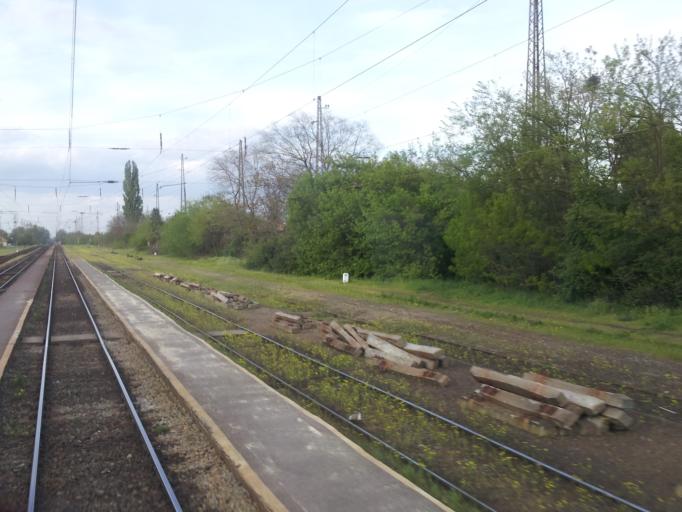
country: HU
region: Budapest
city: Budapest XV. keruelet
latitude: 47.5660
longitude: 19.1127
